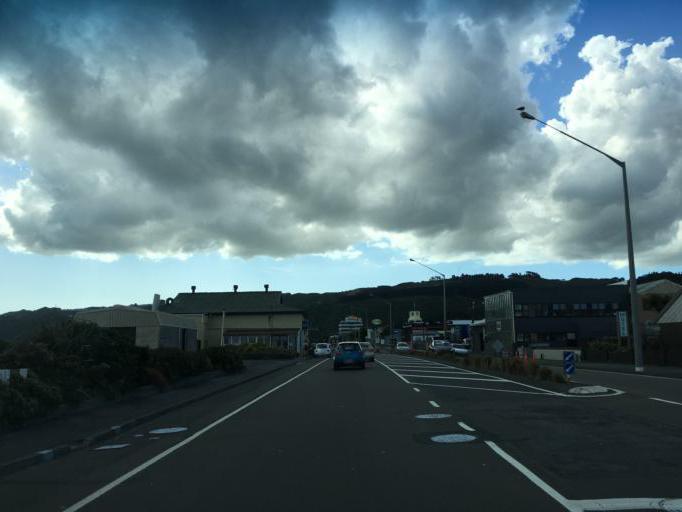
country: NZ
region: Wellington
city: Petone
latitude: -41.2277
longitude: 174.8752
